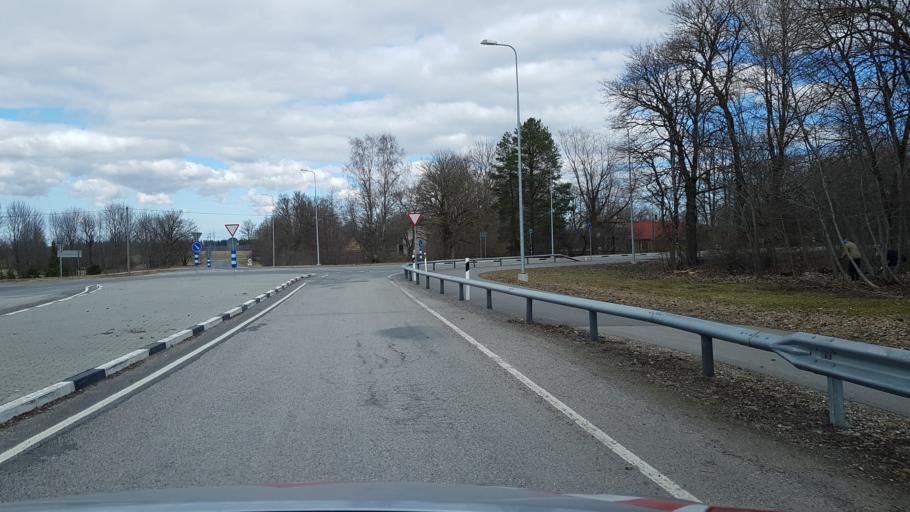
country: EE
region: Laeaene-Virumaa
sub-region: Tamsalu vald
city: Tamsalu
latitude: 59.1731
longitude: 26.1232
